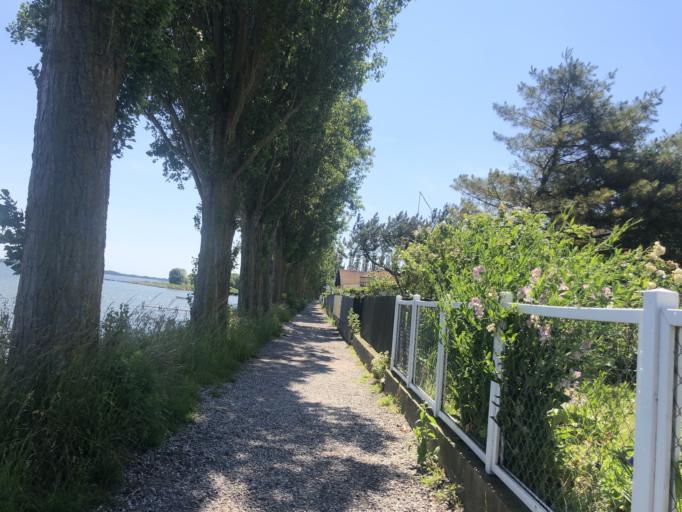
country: DK
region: South Denmark
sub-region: AEro Kommune
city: AEroskobing
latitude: 54.8881
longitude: 10.4137
